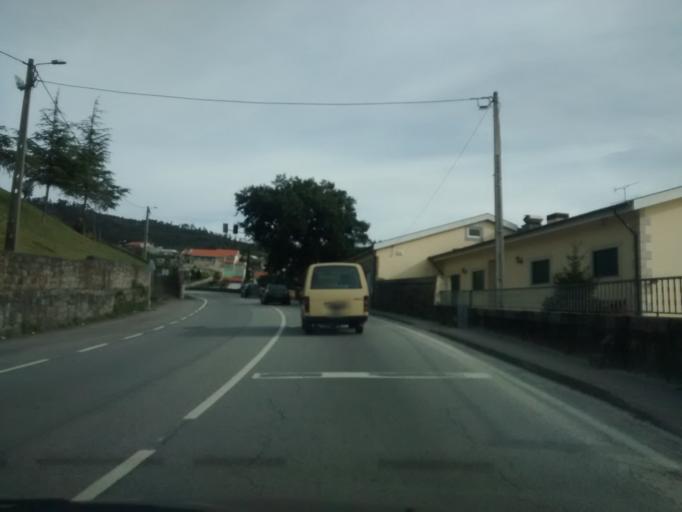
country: PT
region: Braga
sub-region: Braga
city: Braga
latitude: 41.5097
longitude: -8.4189
